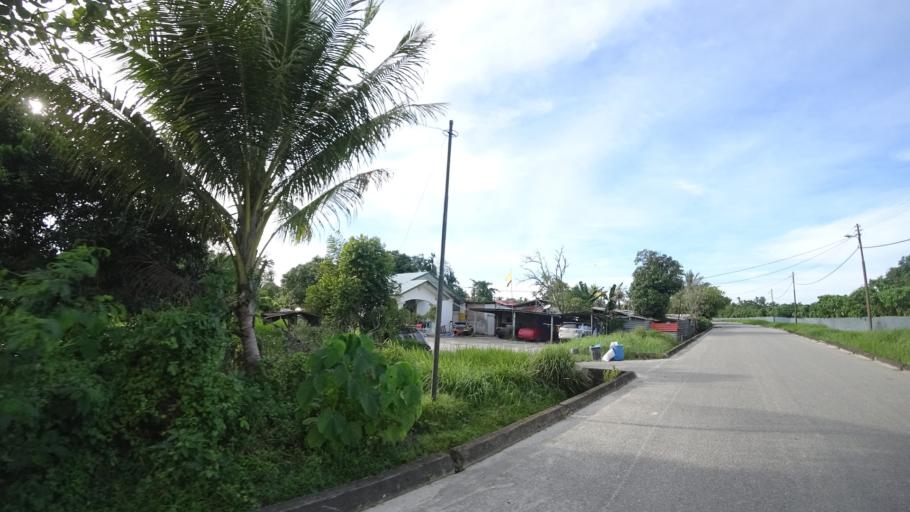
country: BN
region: Brunei and Muara
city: Bandar Seri Begawan
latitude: 4.8209
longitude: 114.8503
